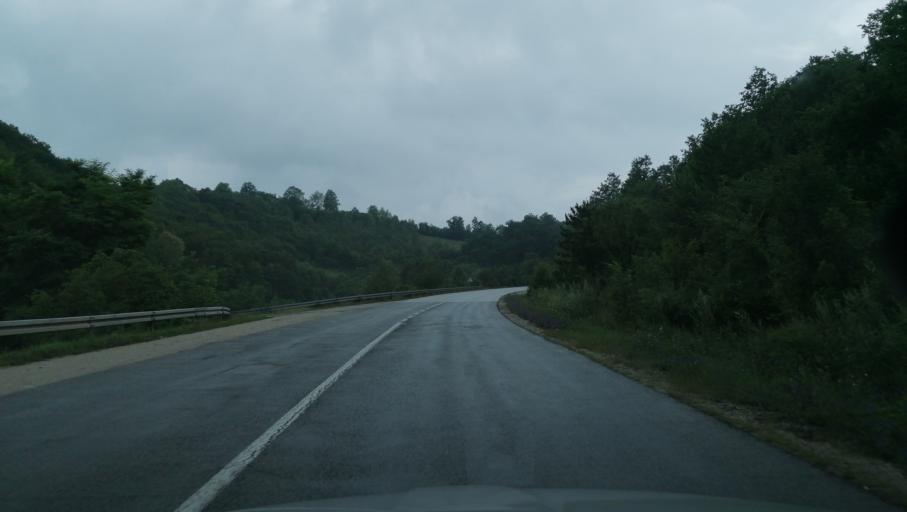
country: RS
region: Central Serbia
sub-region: Zlatiborski Okrug
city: Cajetina
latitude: 43.7892
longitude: 19.7149
